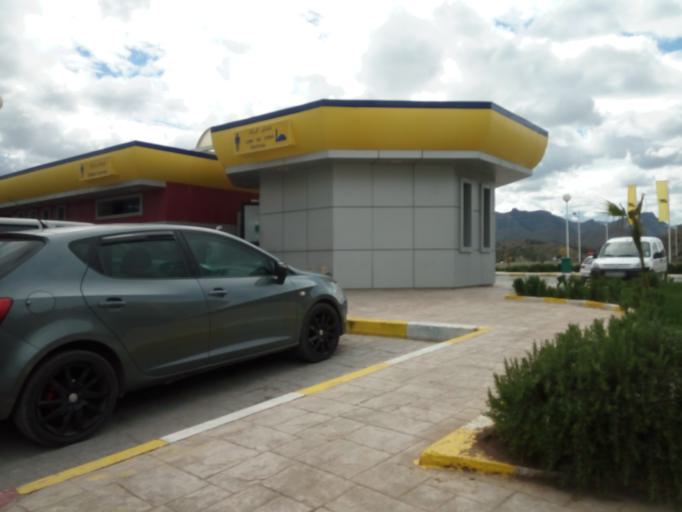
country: DZ
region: Bordj Bou Arreridj
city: Mansourah
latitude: 36.2027
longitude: 4.3996
